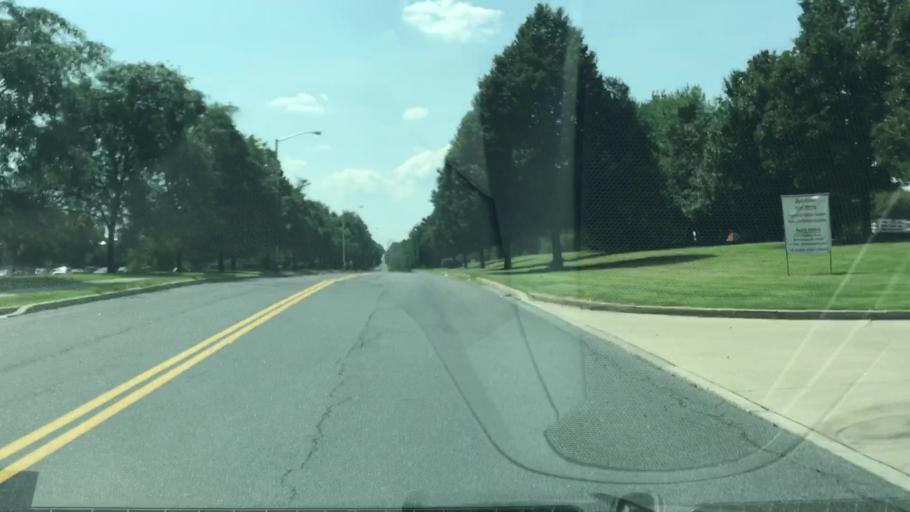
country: US
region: Pennsylvania
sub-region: Northampton County
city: Middletown
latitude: 40.6747
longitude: -75.3636
